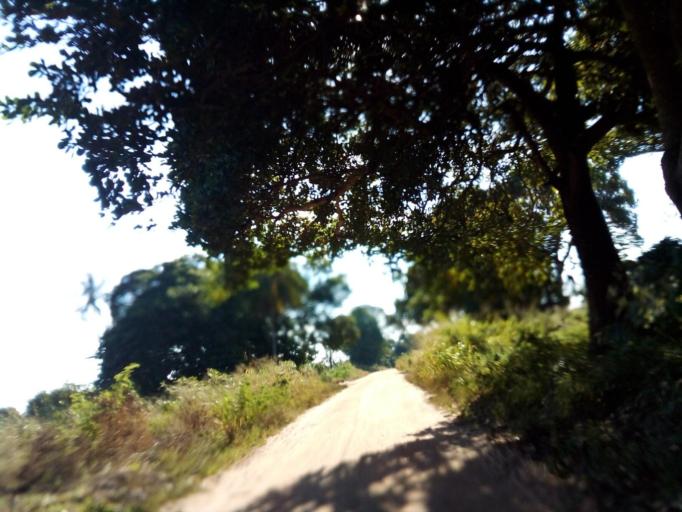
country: MZ
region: Zambezia
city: Quelimane
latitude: -17.5239
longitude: 36.6146
